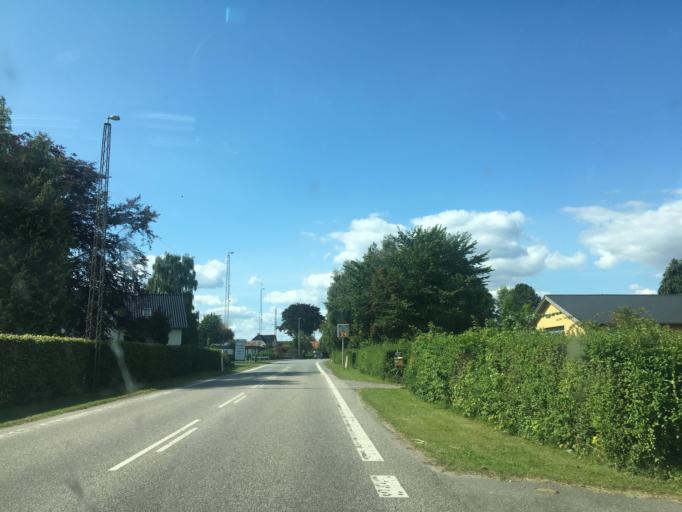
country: DK
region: South Denmark
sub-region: Middelfart Kommune
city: Middelfart
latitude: 55.4895
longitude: 9.7692
